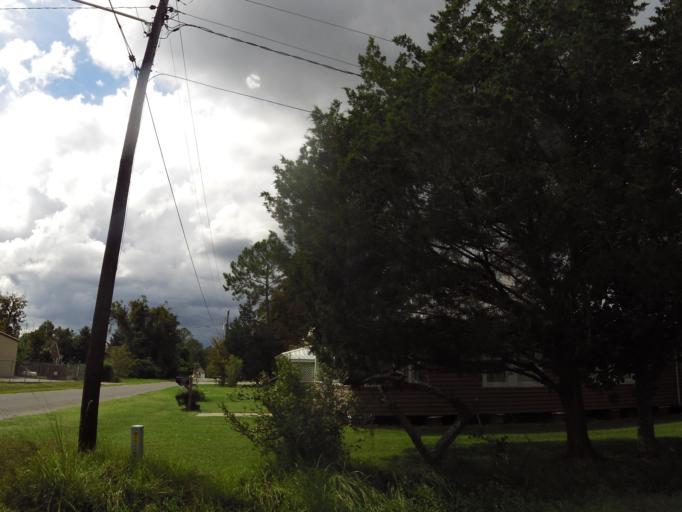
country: US
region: Georgia
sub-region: Brantley County
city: Nahunta
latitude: 31.2037
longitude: -81.9795
